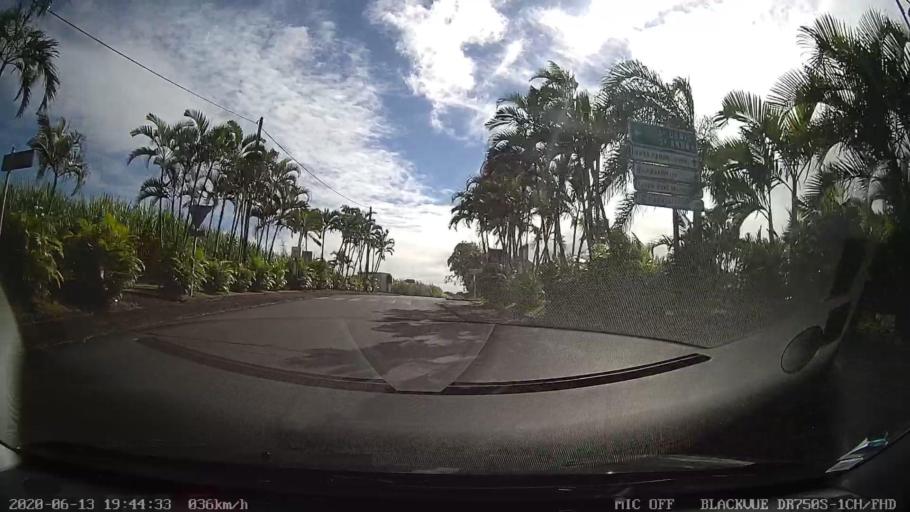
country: RE
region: Reunion
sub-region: Reunion
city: Bras-Panon
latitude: -21.0015
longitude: 55.6764
